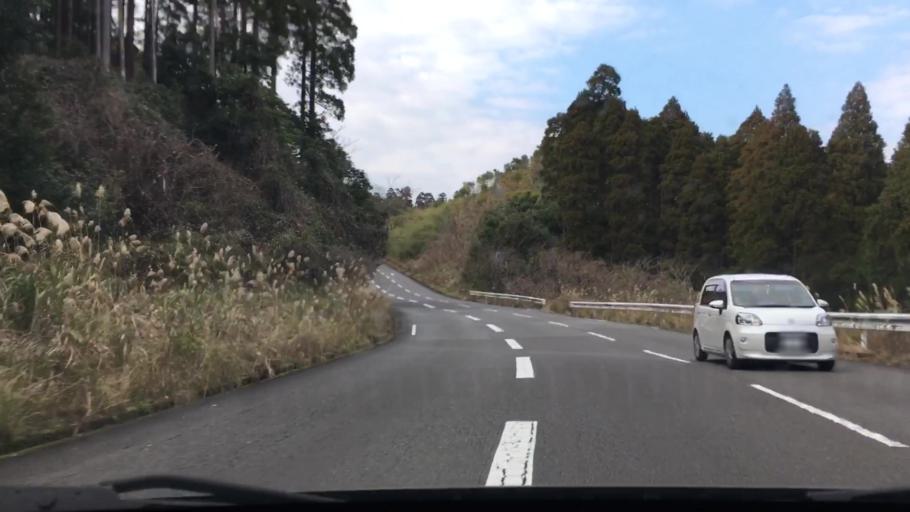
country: JP
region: Miyazaki
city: Nichinan
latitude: 31.6368
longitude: 131.3358
